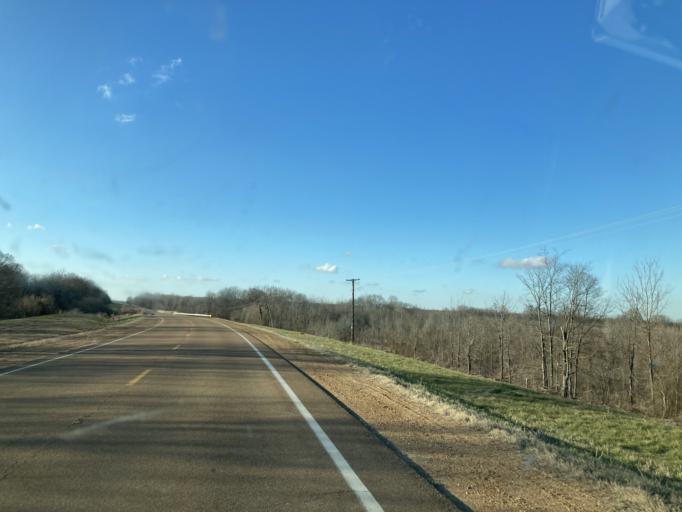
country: US
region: Mississippi
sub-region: Yazoo County
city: Yazoo City
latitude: 32.9177
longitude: -90.5558
